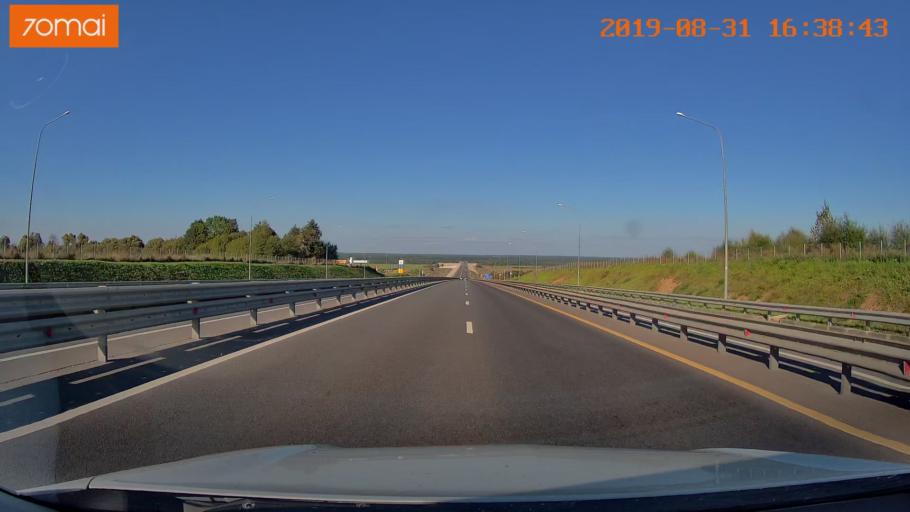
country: RU
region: Kaluga
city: Kurovskoye
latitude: 54.5421
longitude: 36.0108
